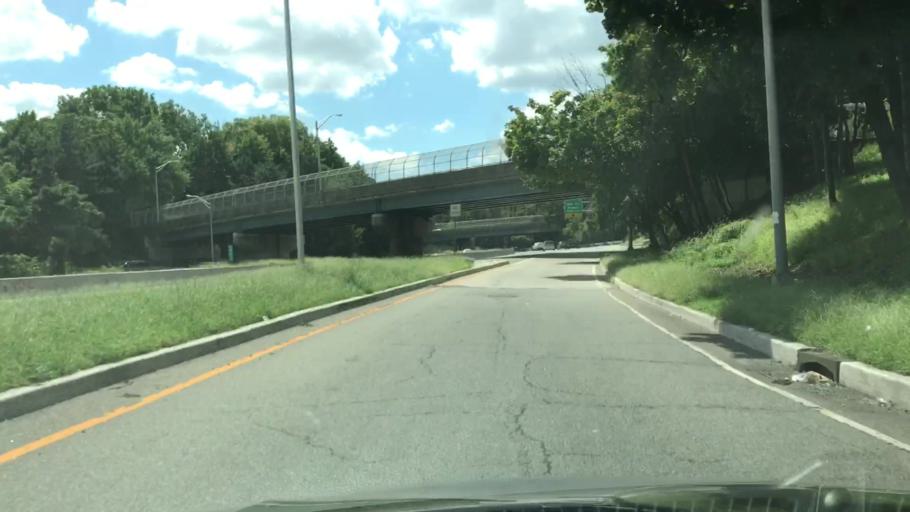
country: US
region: New Jersey
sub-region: Passaic County
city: Passaic
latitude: 40.8572
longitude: -74.1219
